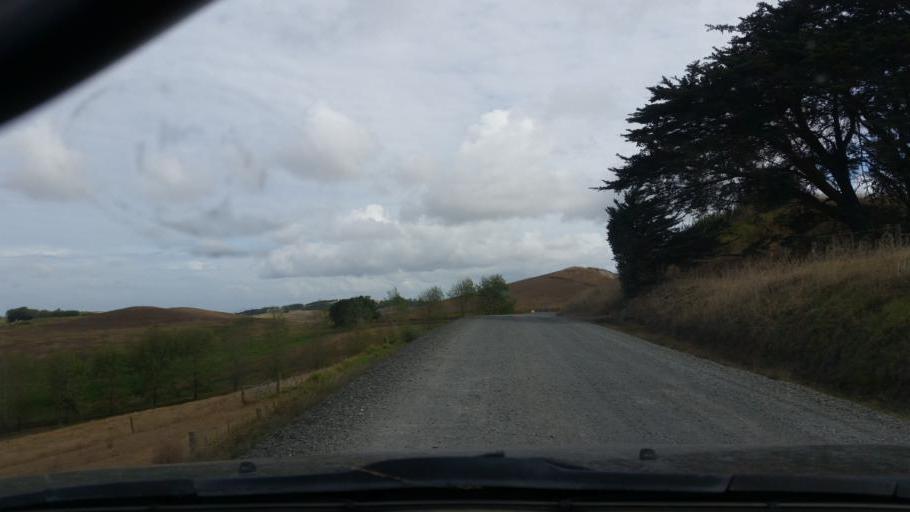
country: NZ
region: Northland
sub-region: Kaipara District
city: Dargaville
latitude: -35.9767
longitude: 173.9524
